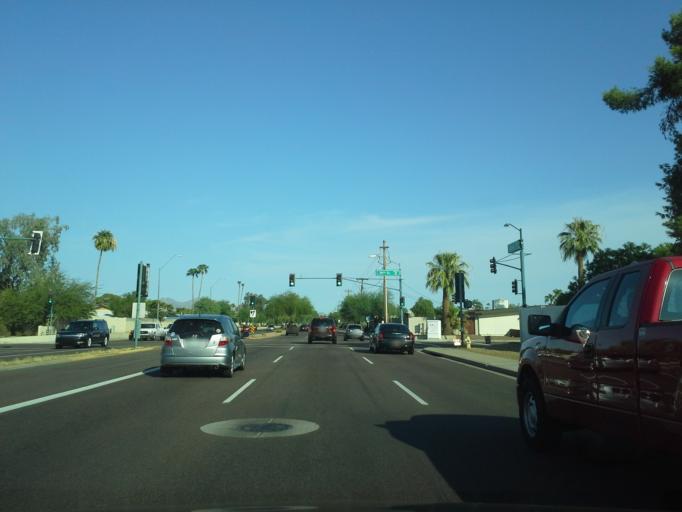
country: US
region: Arizona
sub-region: Maricopa County
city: Paradise Valley
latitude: 33.5969
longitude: -112.0051
